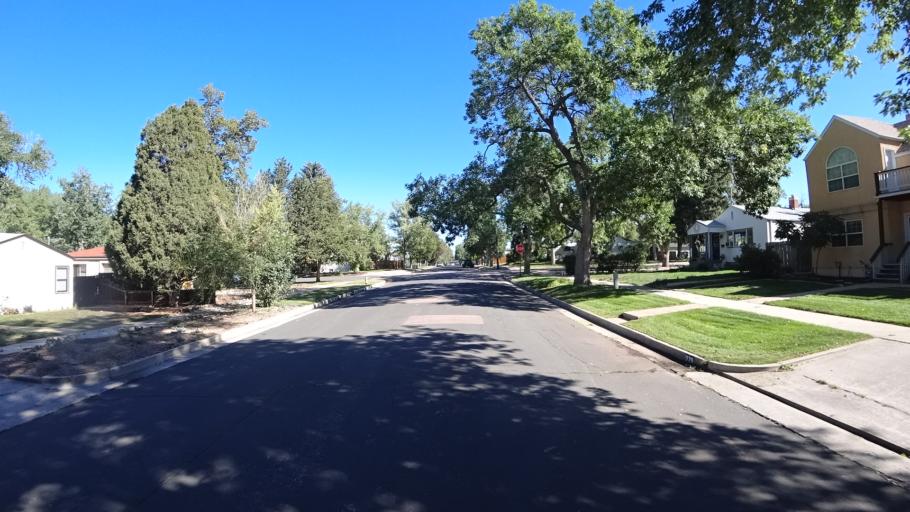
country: US
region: Colorado
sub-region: El Paso County
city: Colorado Springs
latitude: 38.8439
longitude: -104.7987
